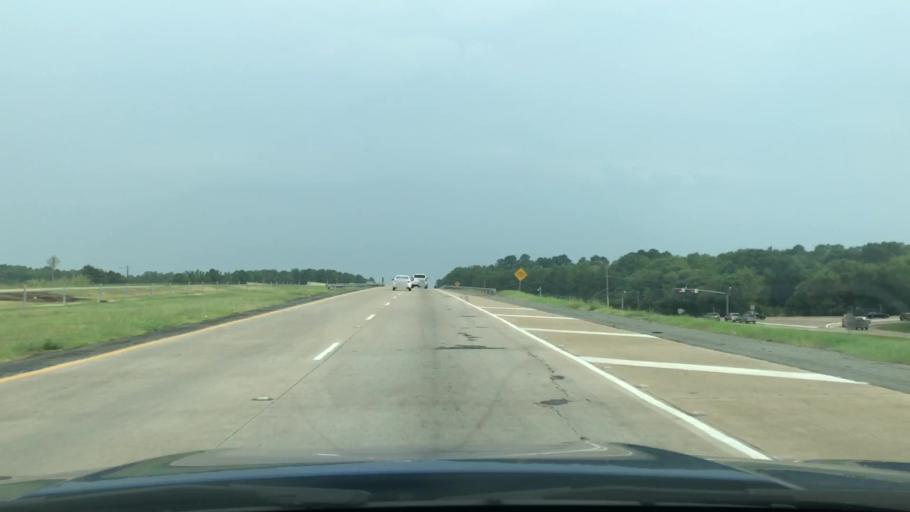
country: US
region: Louisiana
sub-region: Caddo Parish
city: Shreveport
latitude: 32.4440
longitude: -93.8426
